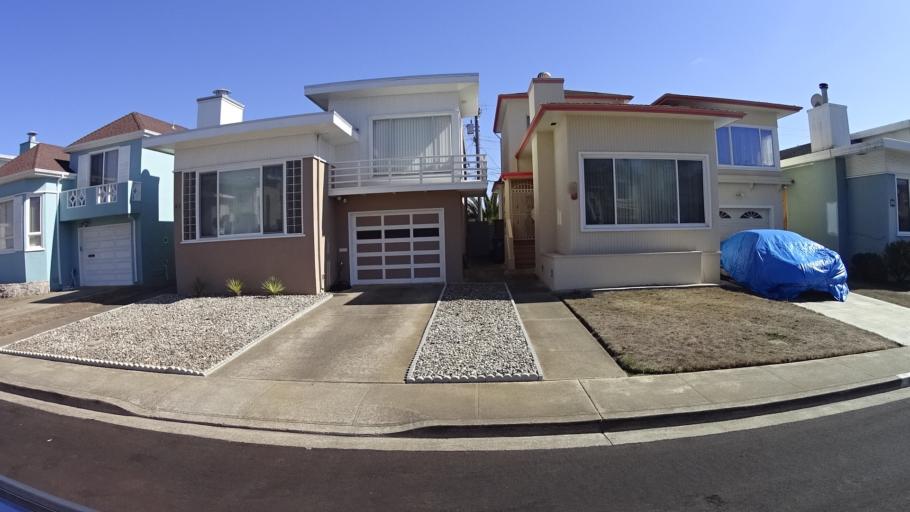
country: US
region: California
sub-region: San Mateo County
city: Broadmoor
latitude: 37.7022
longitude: -122.4887
